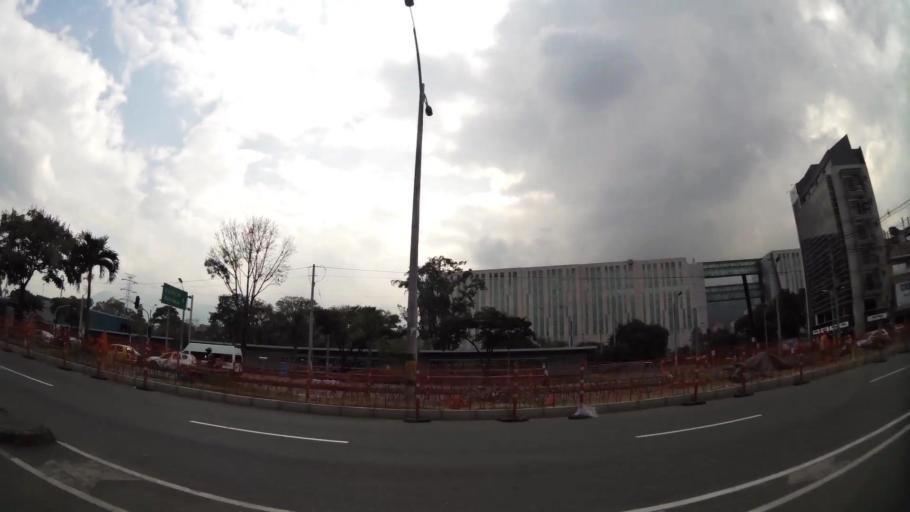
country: CO
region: Antioquia
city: Medellin
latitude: 6.2297
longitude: -75.5773
